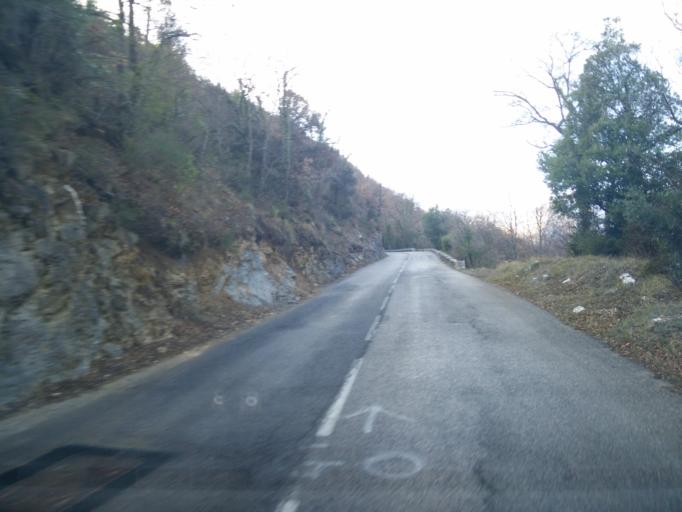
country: FR
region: Provence-Alpes-Cote d'Azur
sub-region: Departement des Alpes-Maritimes
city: Tourrettes-sur-Loup
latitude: 43.7952
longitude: 6.9854
